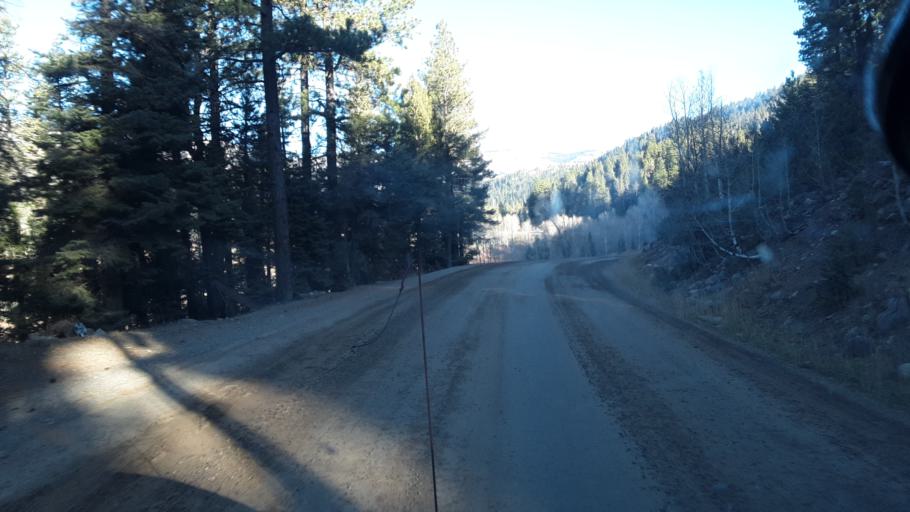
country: US
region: Colorado
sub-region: La Plata County
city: Bayfield
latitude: 37.4080
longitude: -107.6617
